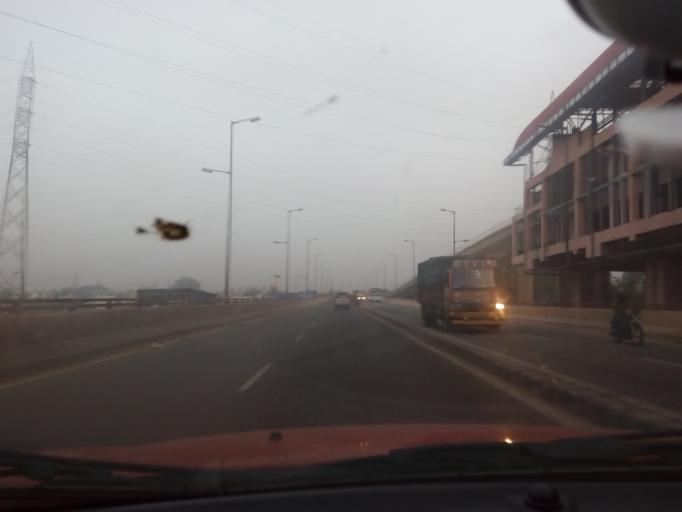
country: IN
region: Karnataka
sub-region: Bangalore Urban
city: Bangalore
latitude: 13.0327
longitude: 77.5332
